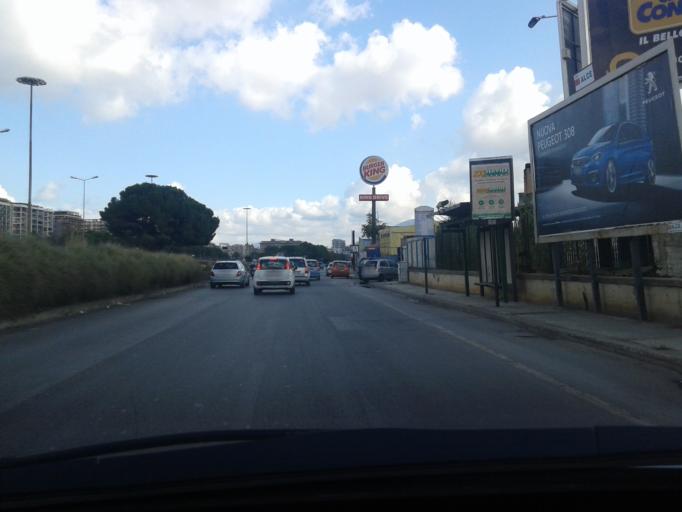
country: IT
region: Sicily
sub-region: Palermo
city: Palermo
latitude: 38.1504
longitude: 13.3239
